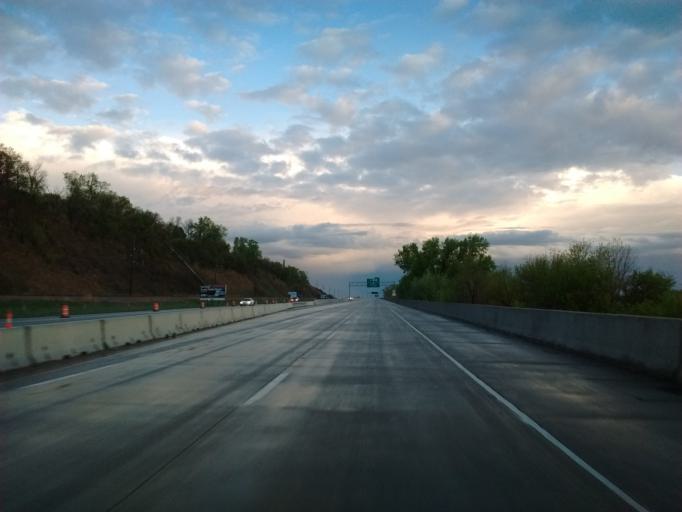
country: US
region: Nebraska
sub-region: Dakota County
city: South Sioux City
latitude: 42.4695
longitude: -96.3816
